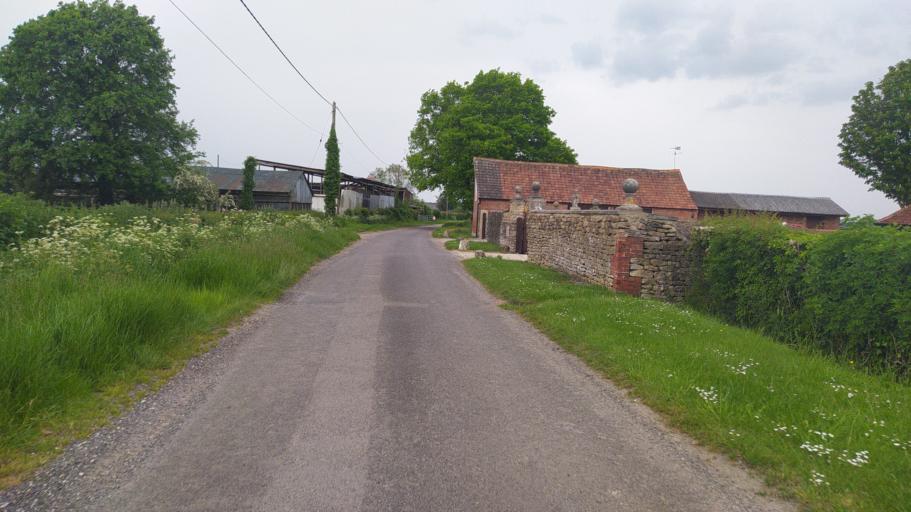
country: GB
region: England
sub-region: Wiltshire
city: Seend
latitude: 51.3443
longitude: -2.0764
